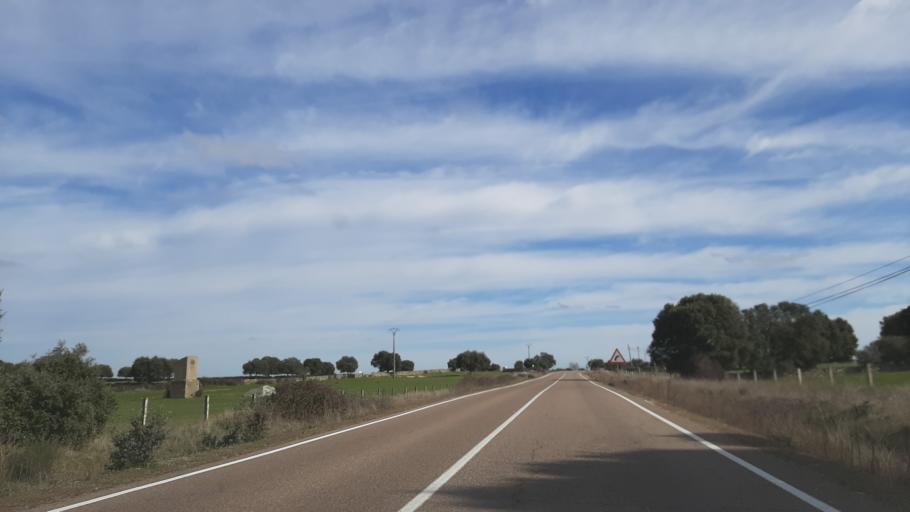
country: ES
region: Castille and Leon
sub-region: Provincia de Salamanca
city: Monleras
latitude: 41.1817
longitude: -6.2207
